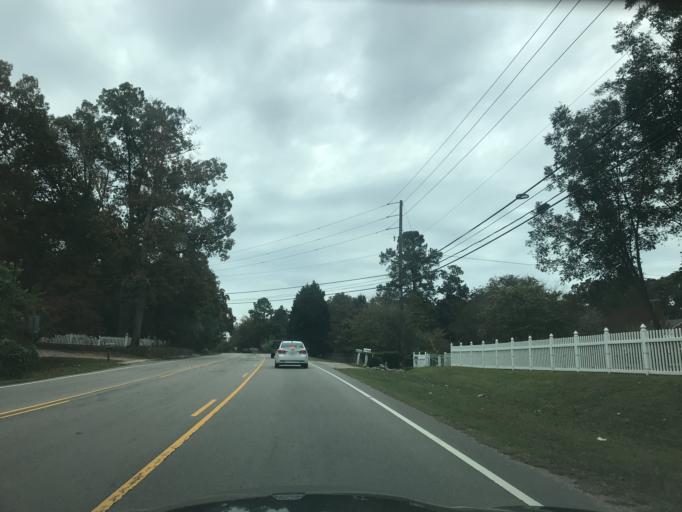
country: US
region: North Carolina
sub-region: Wake County
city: Raleigh
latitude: 35.8689
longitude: -78.5975
